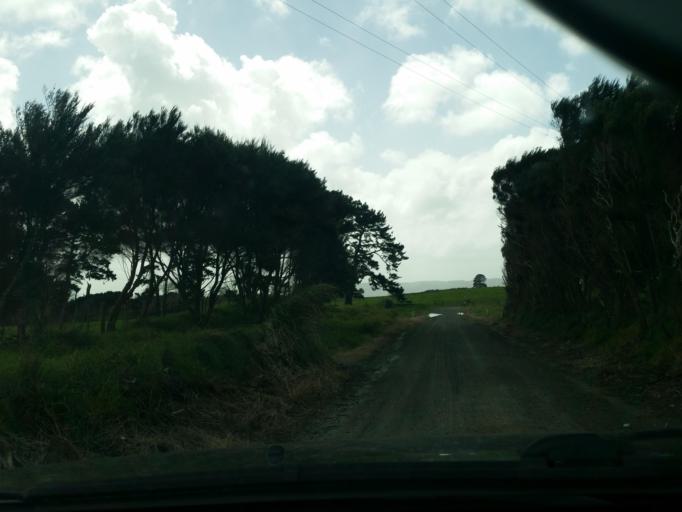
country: NZ
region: Auckland
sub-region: Auckland
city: Wellsford
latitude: -36.2696
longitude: 174.1279
